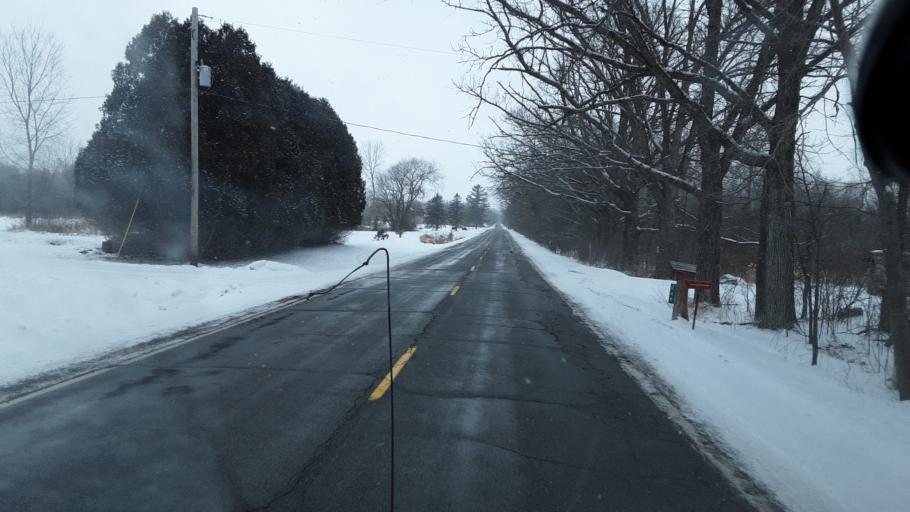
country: US
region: Michigan
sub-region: Ingham County
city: Leslie
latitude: 42.4716
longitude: -84.3414
